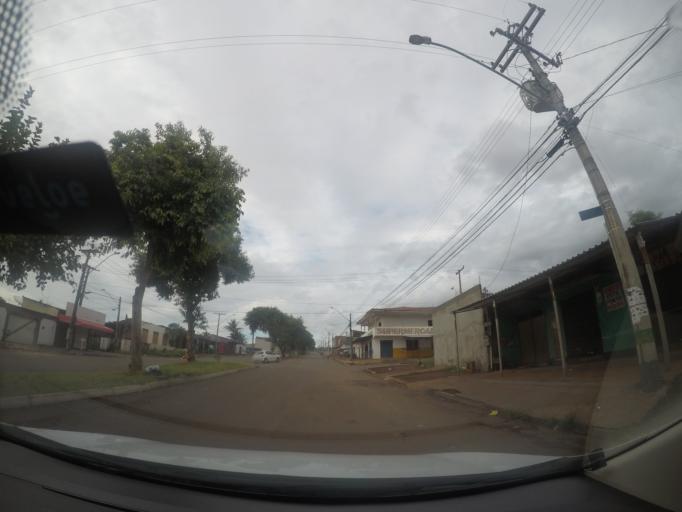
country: BR
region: Goias
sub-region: Goiania
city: Goiania
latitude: -16.5976
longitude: -49.3043
